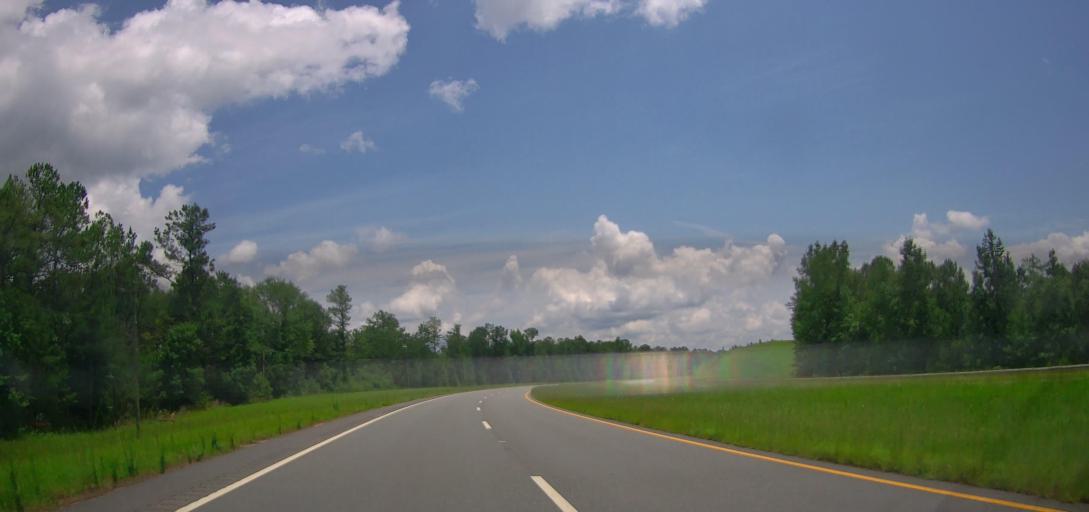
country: US
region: Georgia
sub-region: Upson County
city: Thomaston
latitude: 32.8179
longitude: -84.2915
